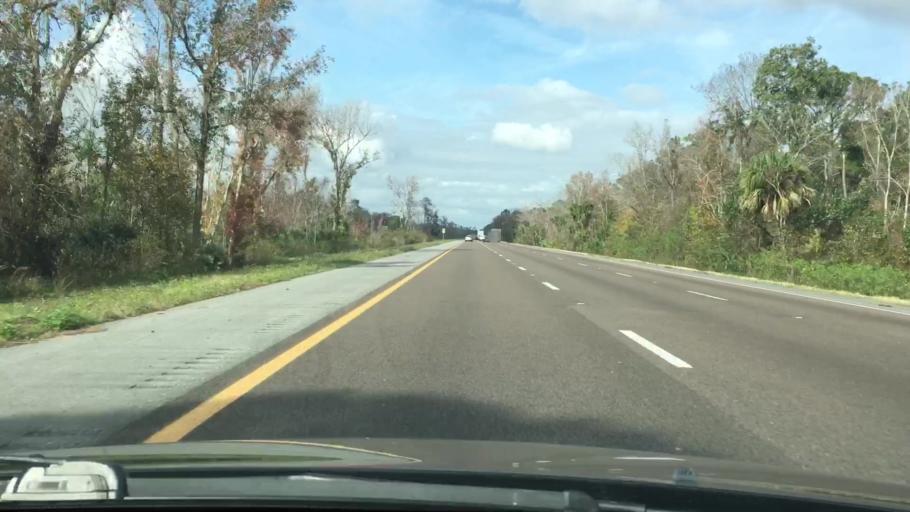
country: US
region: Florida
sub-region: Volusia County
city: Oak Hill
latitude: 28.8907
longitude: -80.9271
